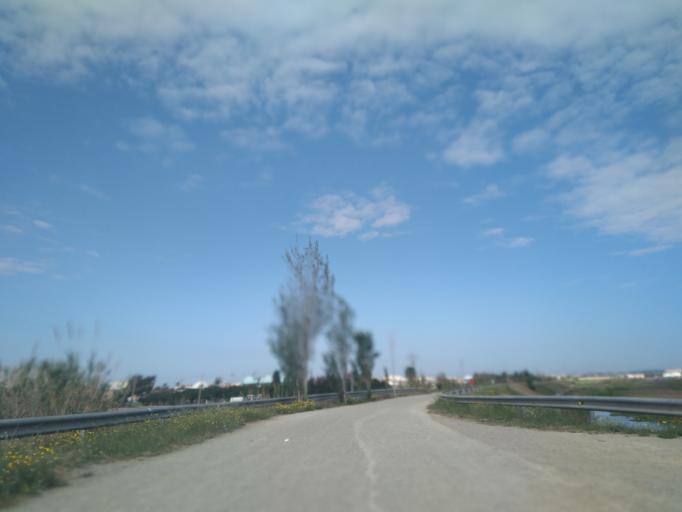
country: ES
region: Valencia
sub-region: Provincia de Valencia
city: Alboraya
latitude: 39.5020
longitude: -0.3296
